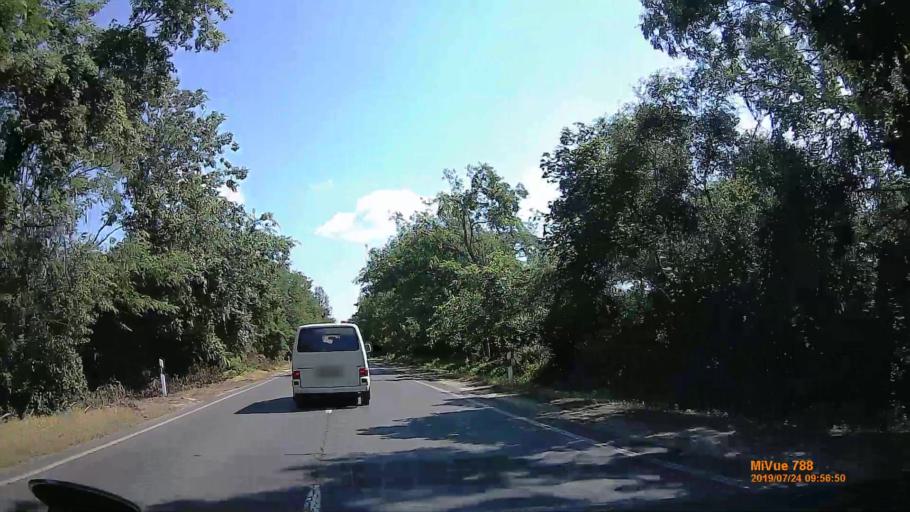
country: HU
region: Szabolcs-Szatmar-Bereg
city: Nyirmada
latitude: 48.0682
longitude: 22.2304
